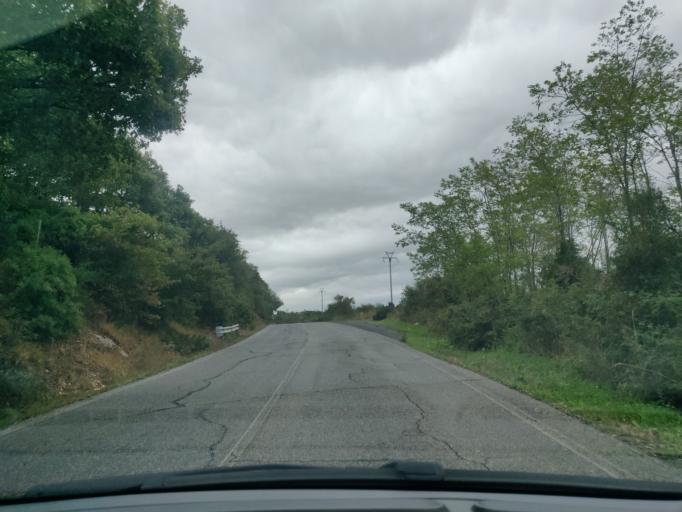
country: IT
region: Latium
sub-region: Citta metropolitana di Roma Capitale
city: Allumiere
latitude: 42.1257
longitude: 11.8600
